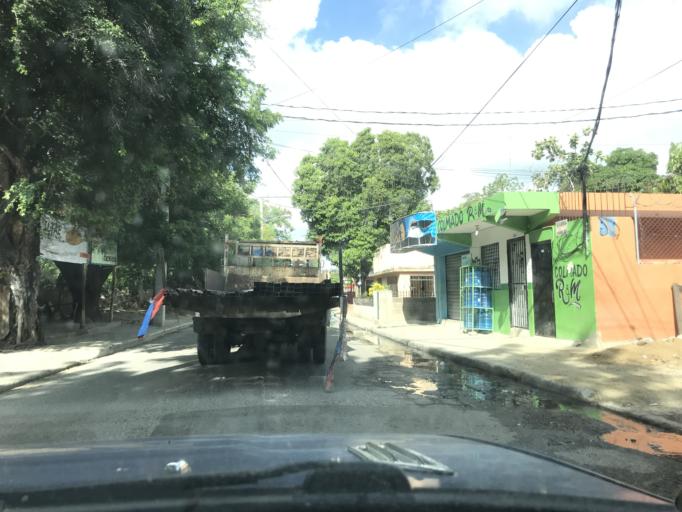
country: DO
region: Santiago
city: Santiago de los Caballeros
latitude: 19.4543
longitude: -70.7255
